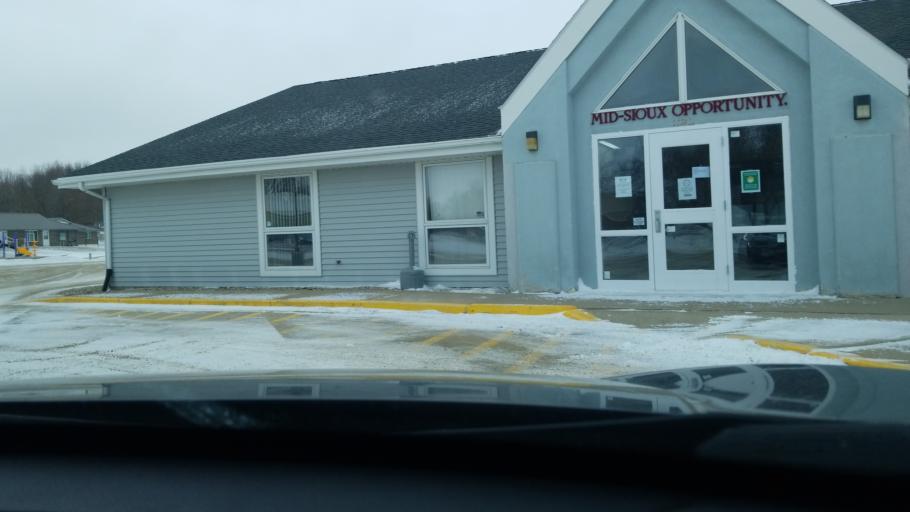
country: US
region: Iowa
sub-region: Lyon County
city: Rock Rapids
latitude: 43.4304
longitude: -96.1579
